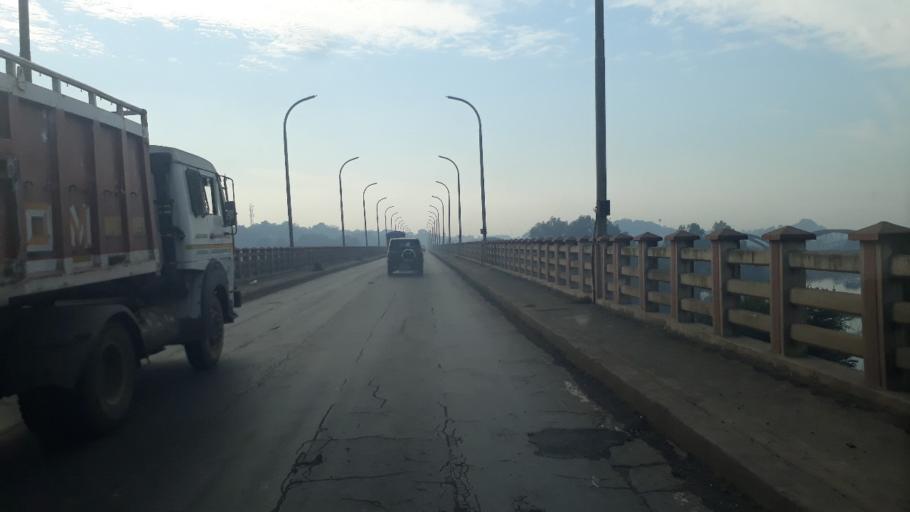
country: IN
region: Maharashtra
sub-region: Raigarh
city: Pen
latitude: 18.8404
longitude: 73.0931
